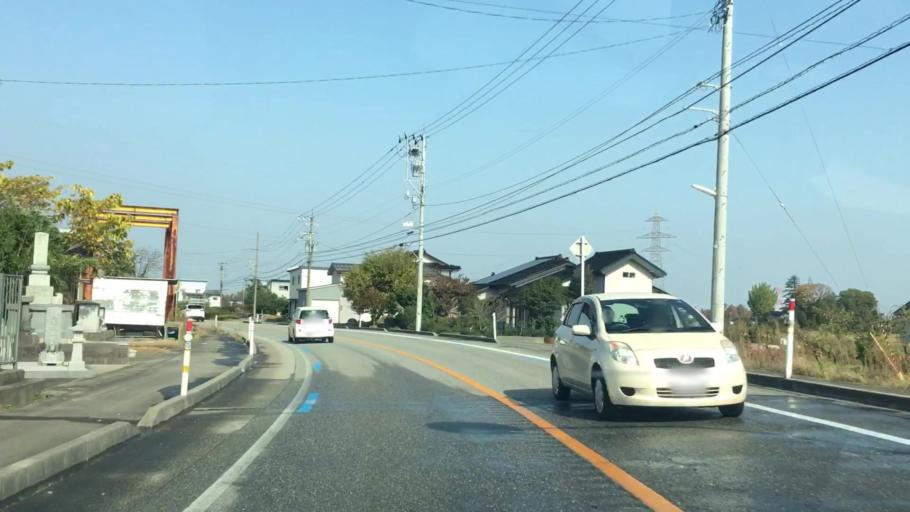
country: JP
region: Toyama
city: Yatsuomachi-higashikumisaka
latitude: 36.6182
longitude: 137.1929
